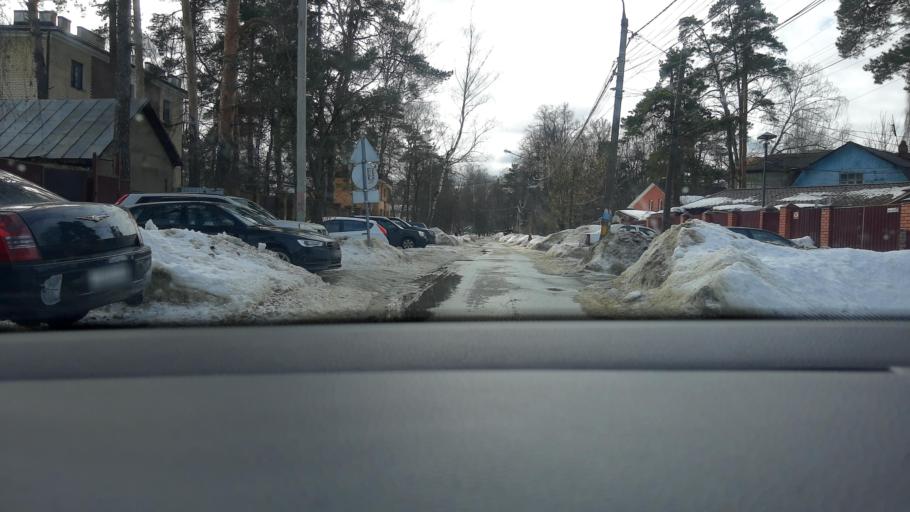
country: RU
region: Moskovskaya
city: Druzhba
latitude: 55.8976
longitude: 37.7466
